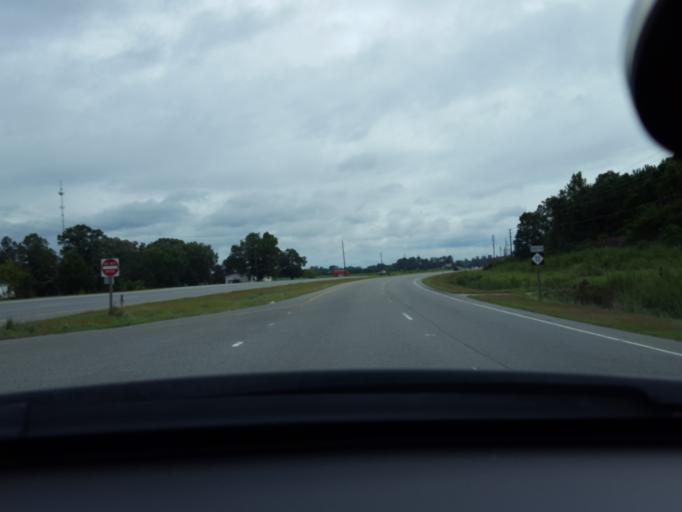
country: US
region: North Carolina
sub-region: Pitt County
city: Ayden
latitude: 35.4500
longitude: -77.4298
